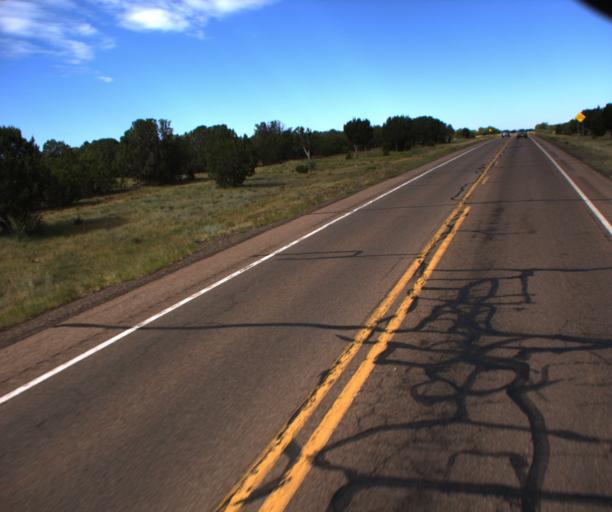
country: US
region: Arizona
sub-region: Navajo County
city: Show Low
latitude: 34.2679
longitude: -109.9405
